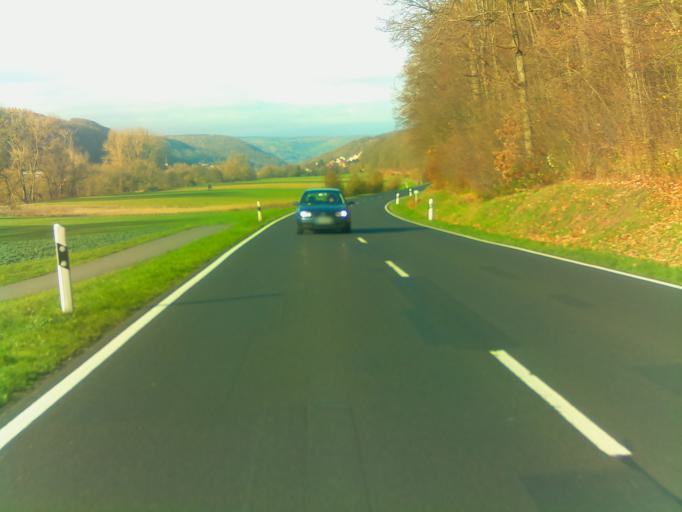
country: DE
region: Bavaria
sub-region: Regierungsbezirk Unterfranken
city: Hafenlohr
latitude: 49.8729
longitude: 9.6074
